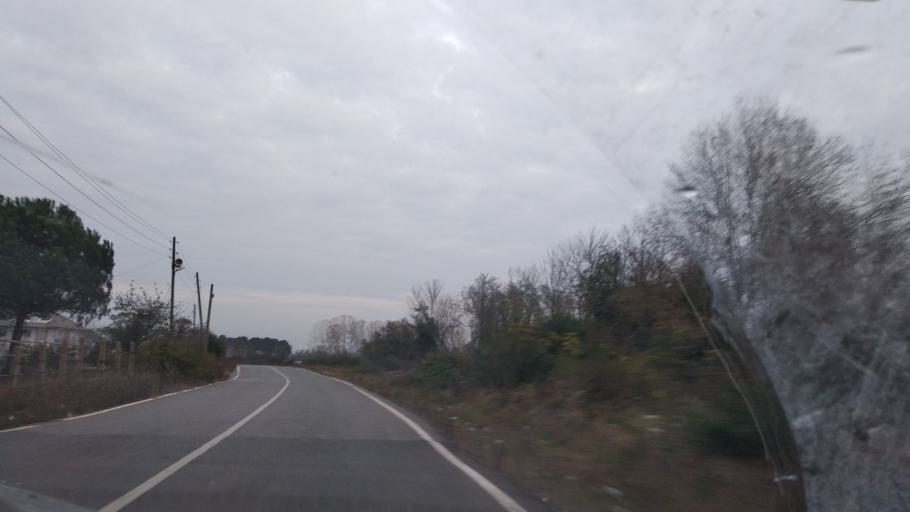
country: TR
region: Sakarya
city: Karasu
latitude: 41.0841
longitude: 30.7348
